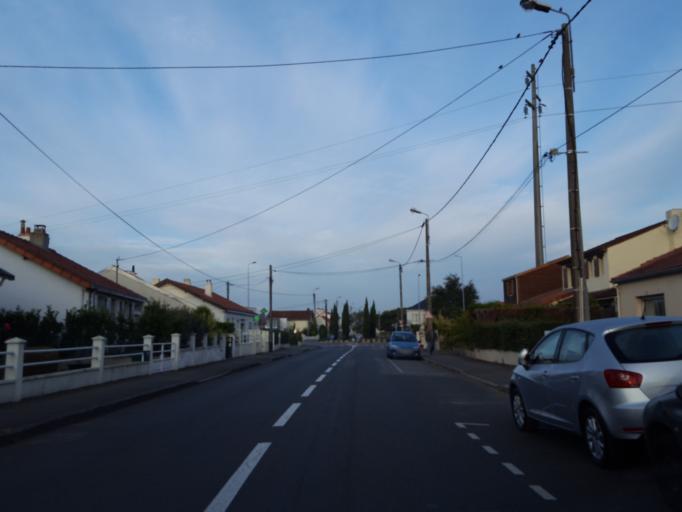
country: FR
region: Pays de la Loire
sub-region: Departement de la Loire-Atlantique
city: Saint-Sebastien-sur-Loire
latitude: 47.1993
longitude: -1.4986
